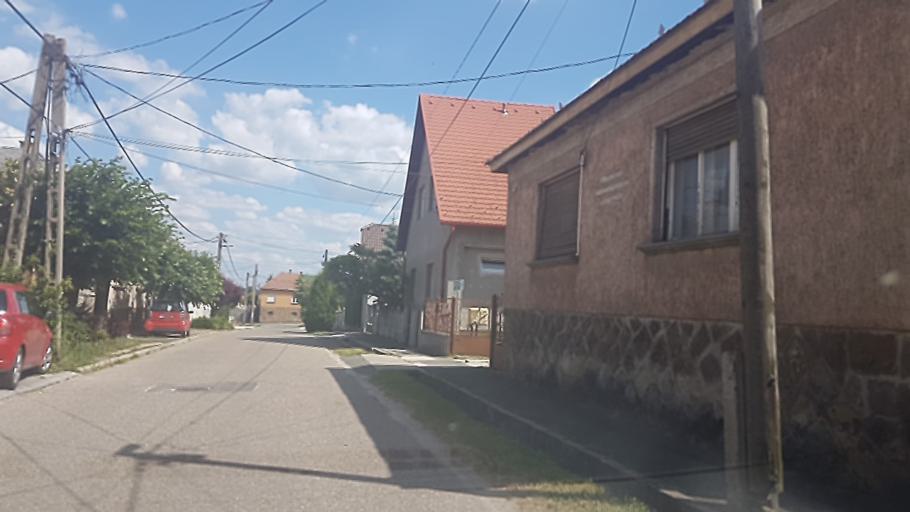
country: HU
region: Pest
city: Pilisszentivan
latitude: 47.6095
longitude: 18.8932
